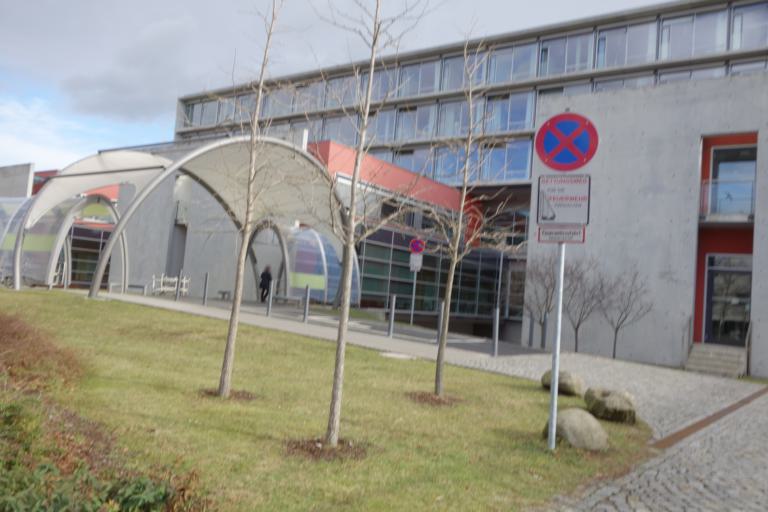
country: DE
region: Saxony
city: Albertstadt
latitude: 51.0576
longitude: 13.7792
